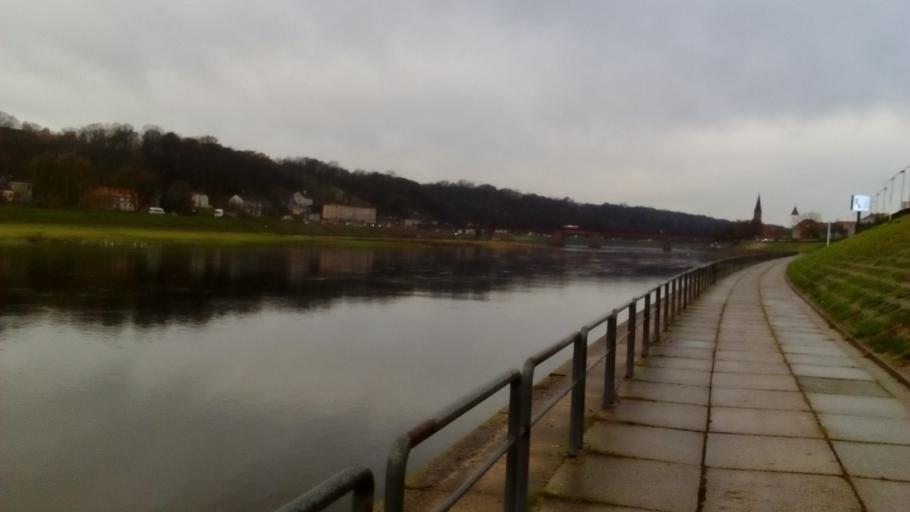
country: LT
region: Kauno apskritis
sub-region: Kaunas
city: Kaunas
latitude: 54.8940
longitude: 23.8984
